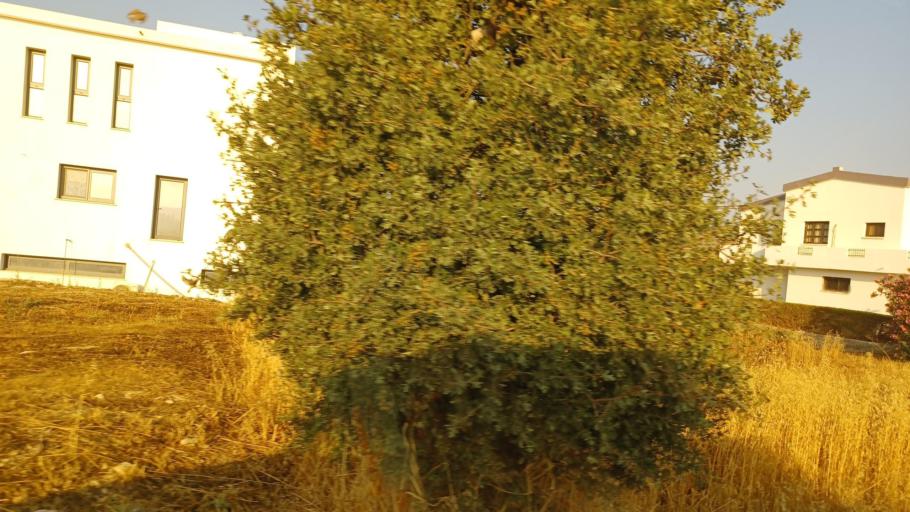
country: CY
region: Larnaka
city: Pyla
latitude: 35.0076
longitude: 33.6868
